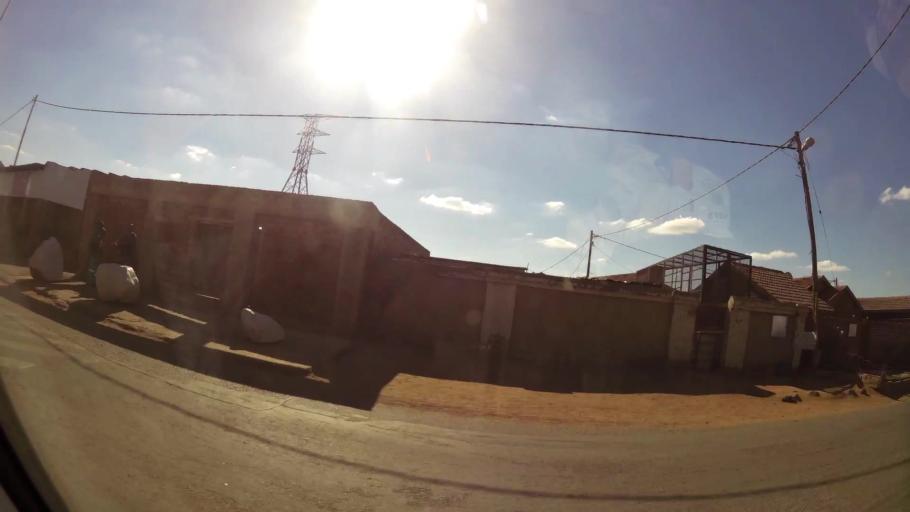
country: ZA
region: Gauteng
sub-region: City of Tshwane Metropolitan Municipality
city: Cullinan
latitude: -25.7139
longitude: 28.3986
